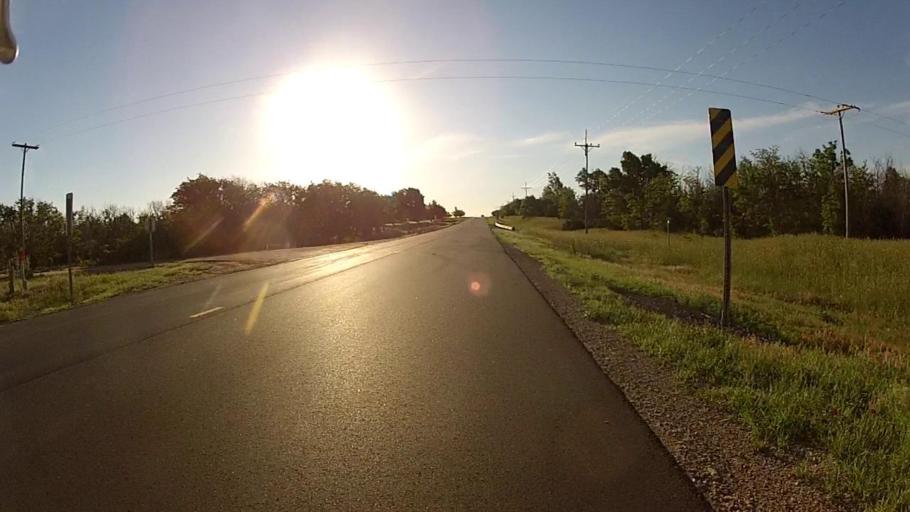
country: US
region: Kansas
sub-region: Comanche County
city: Coldwater
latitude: 37.2813
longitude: -99.2024
